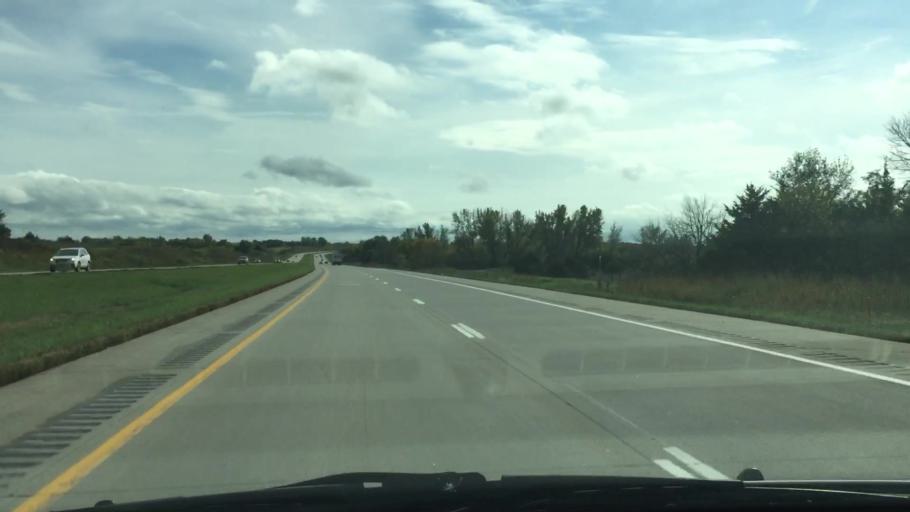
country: US
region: Iowa
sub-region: Clarke County
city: Osceola
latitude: 40.9129
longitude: -93.7975
